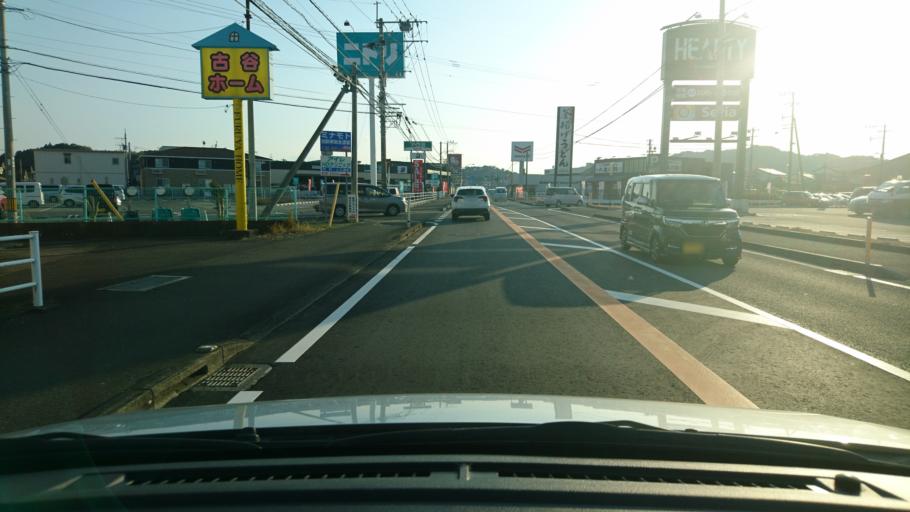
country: JP
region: Miyazaki
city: Miyazaki-shi
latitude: 31.9780
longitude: 131.4443
